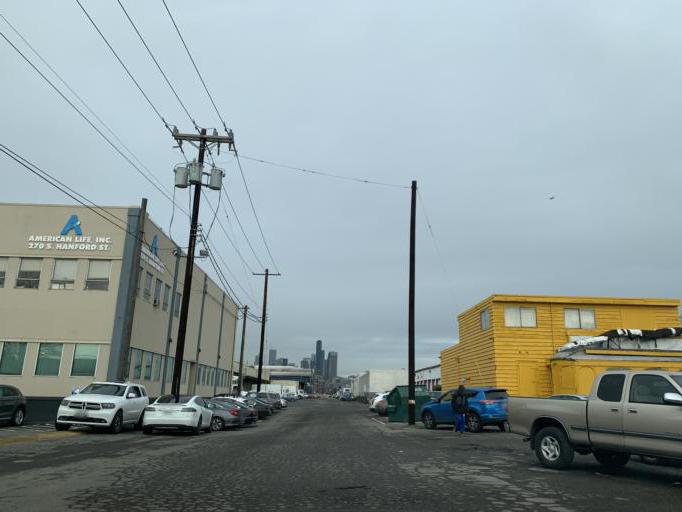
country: US
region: Washington
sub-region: King County
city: Seattle
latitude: 47.5755
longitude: -122.3300
